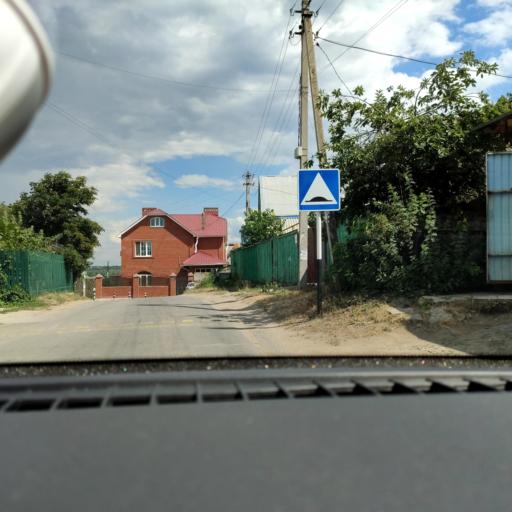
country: RU
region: Samara
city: Volzhskiy
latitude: 53.4282
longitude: 50.1316
